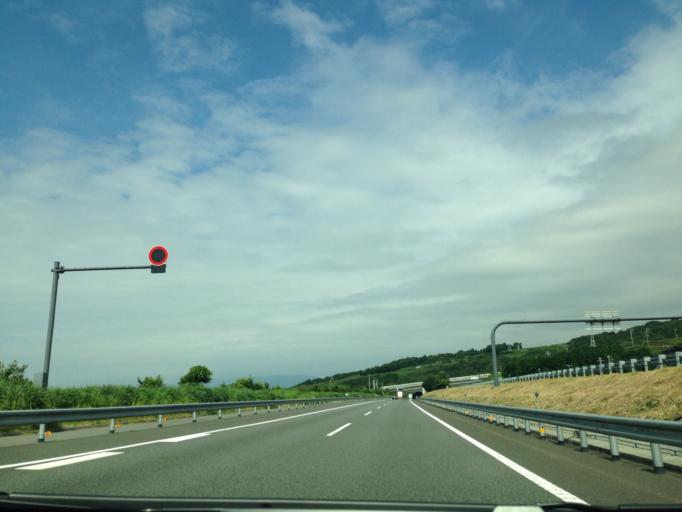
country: JP
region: Shizuoka
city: Numazu
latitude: 35.1538
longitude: 138.8021
